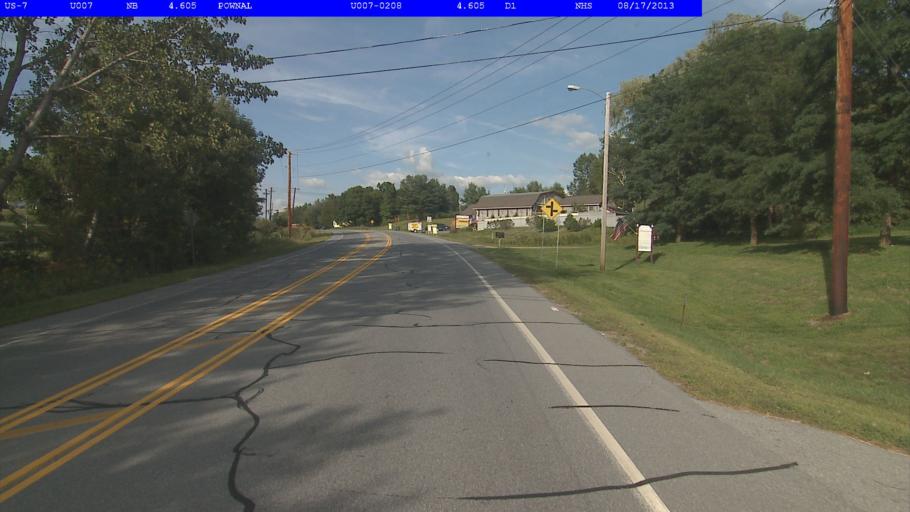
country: US
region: Massachusetts
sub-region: Berkshire County
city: Williamstown
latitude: 42.7932
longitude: -73.2243
